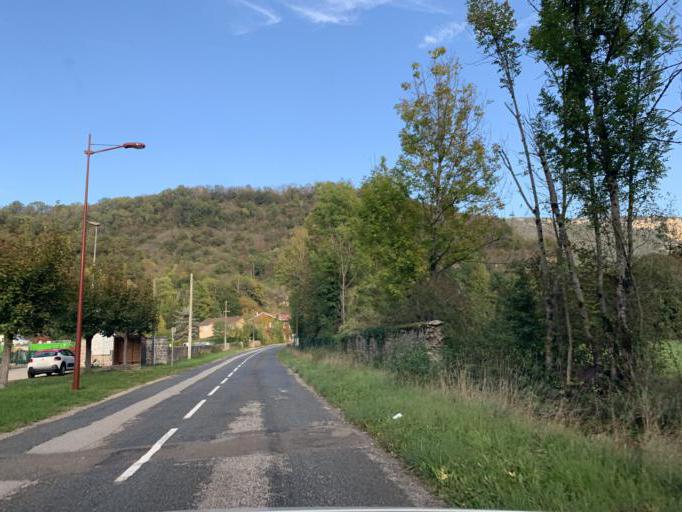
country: FR
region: Rhone-Alpes
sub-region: Departement de l'Ain
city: Saint-Rambert-en-Bugey
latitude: 45.9513
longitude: 5.4626
